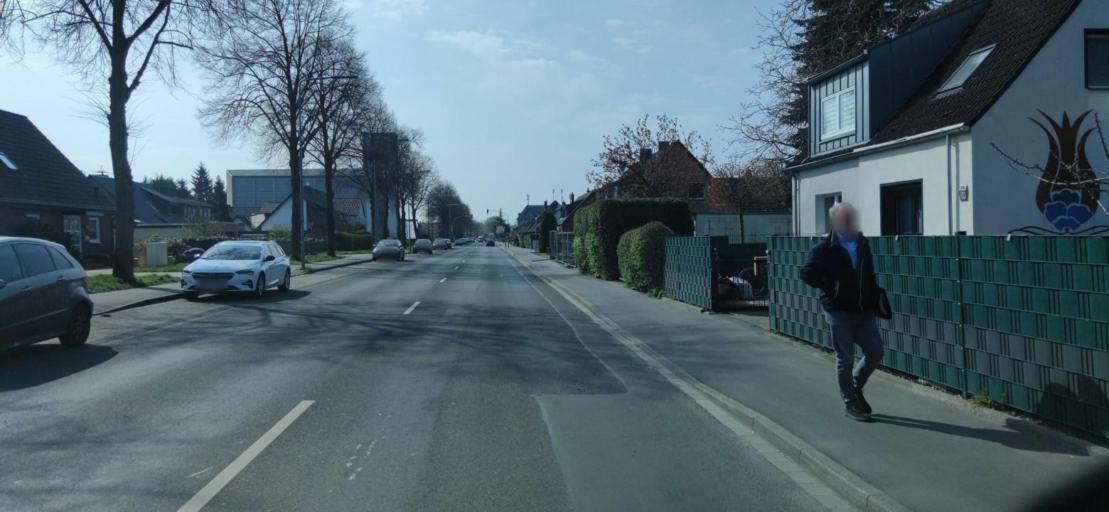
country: DE
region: North Rhine-Westphalia
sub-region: Regierungsbezirk Dusseldorf
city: Erkrath
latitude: 51.2175
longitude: 6.8488
